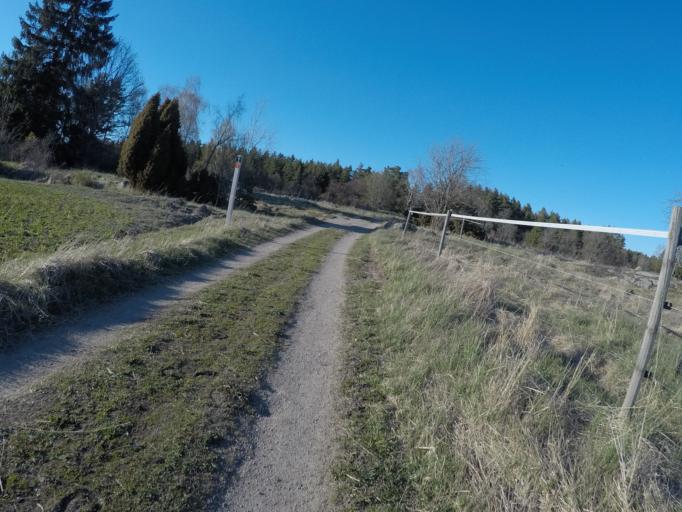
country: SE
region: Soedermanland
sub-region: Eskilstuna Kommun
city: Eskilstuna
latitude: 59.4031
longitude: 16.5222
